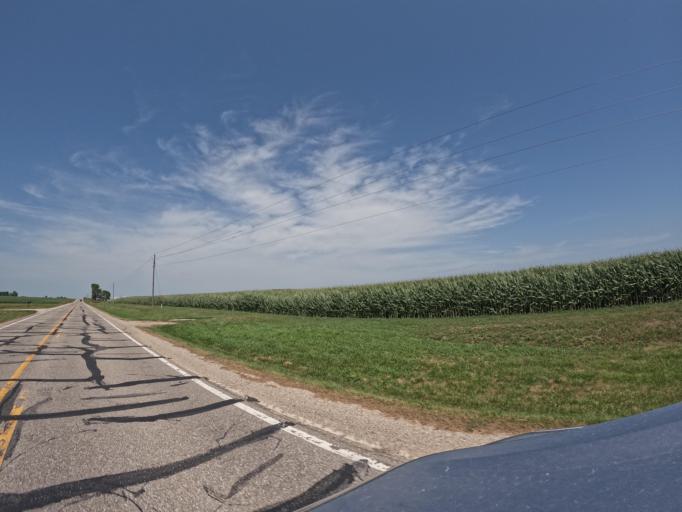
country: US
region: Iowa
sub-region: Henry County
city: Mount Pleasant
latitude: 40.9867
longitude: -91.6123
